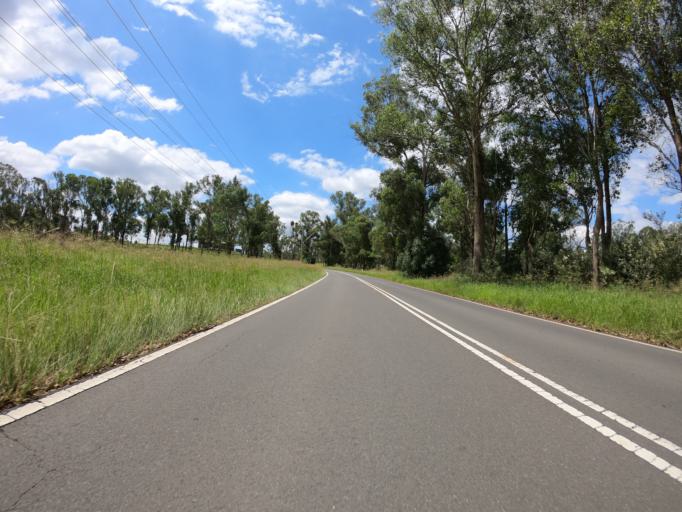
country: AU
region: New South Wales
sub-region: Penrith Municipality
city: Mulgoa
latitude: -33.8289
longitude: 150.6639
